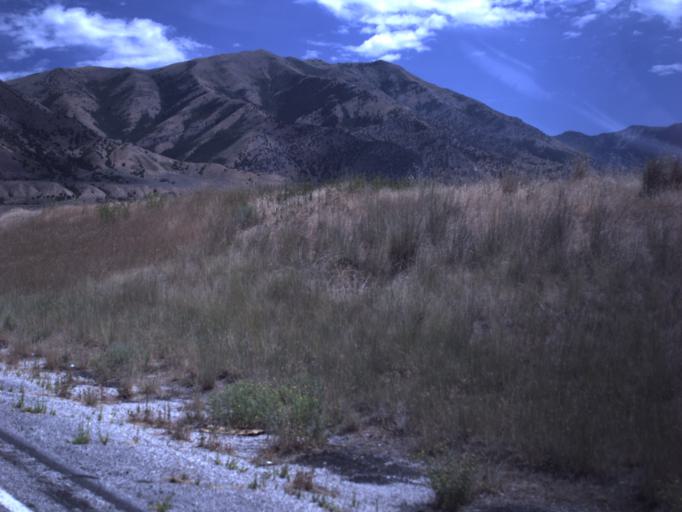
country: US
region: Utah
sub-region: Box Elder County
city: Elwood
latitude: 41.7144
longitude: -112.1095
